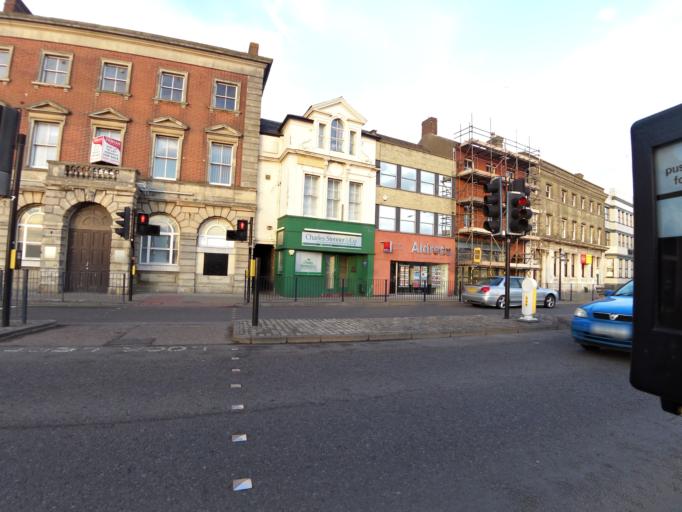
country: GB
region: England
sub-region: Norfolk
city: Great Yarmouth
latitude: 52.6071
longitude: 1.7235
